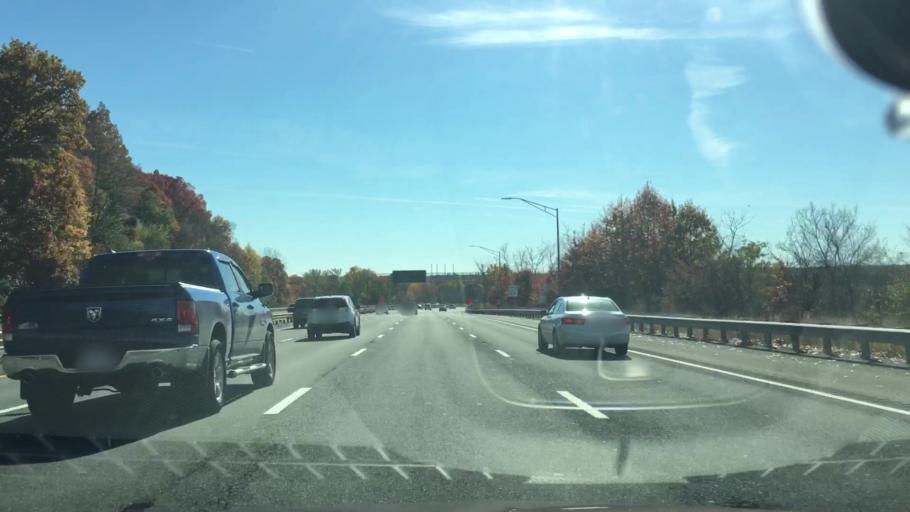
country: US
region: Massachusetts
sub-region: Hampden County
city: Chicopee
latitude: 42.1262
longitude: -72.6084
